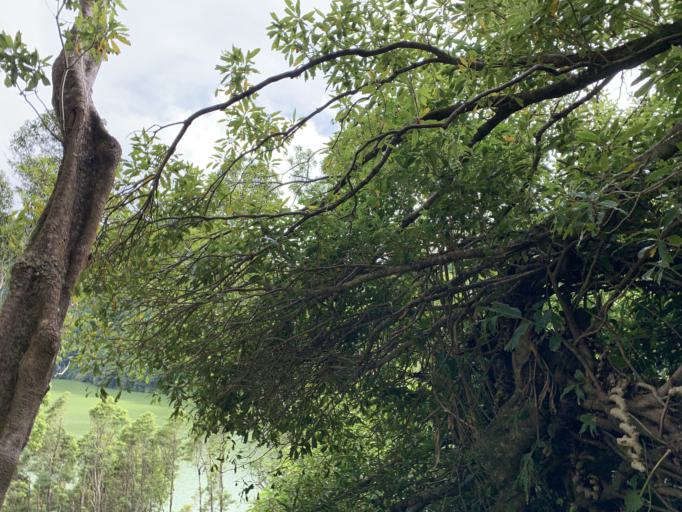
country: PT
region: Azores
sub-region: Ponta Delgada
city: Arrifes
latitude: 37.8523
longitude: -25.7738
